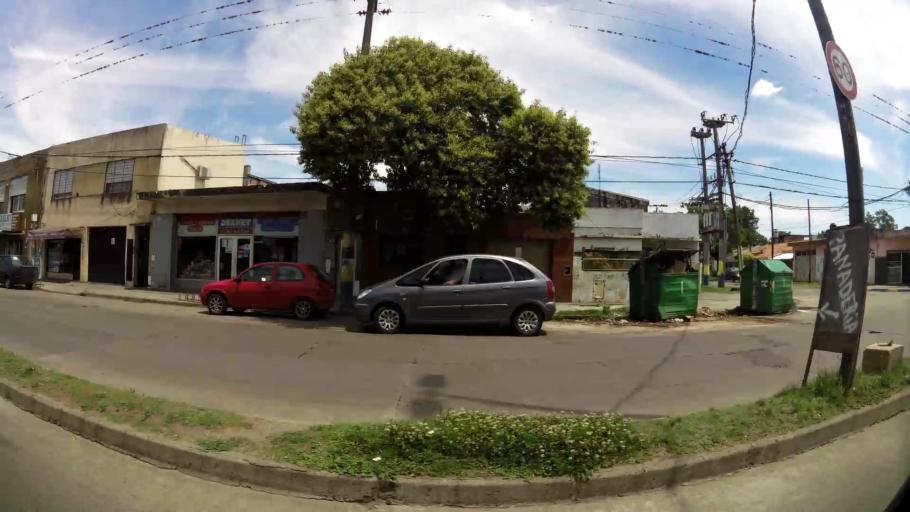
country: AR
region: Santa Fe
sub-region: Departamento de Rosario
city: Rosario
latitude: -32.9872
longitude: -60.6284
